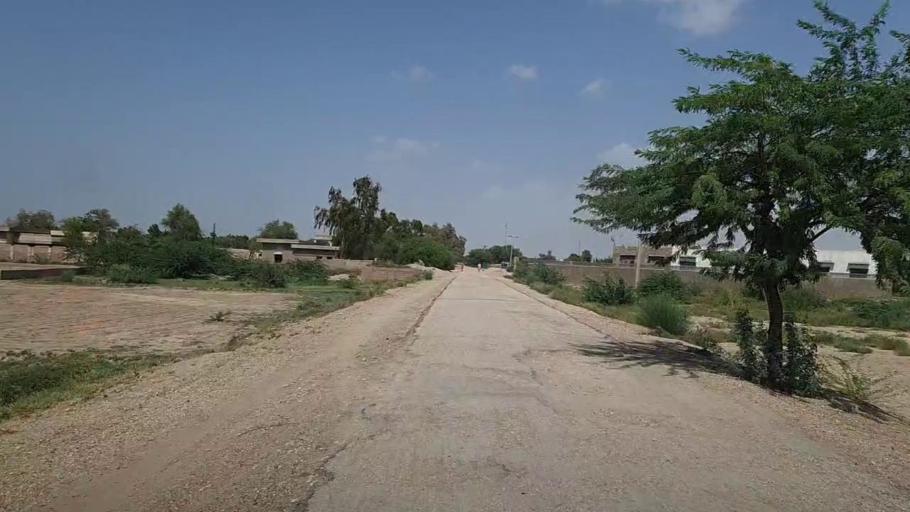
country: PK
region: Sindh
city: Pad Idan
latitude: 26.8070
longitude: 68.3837
